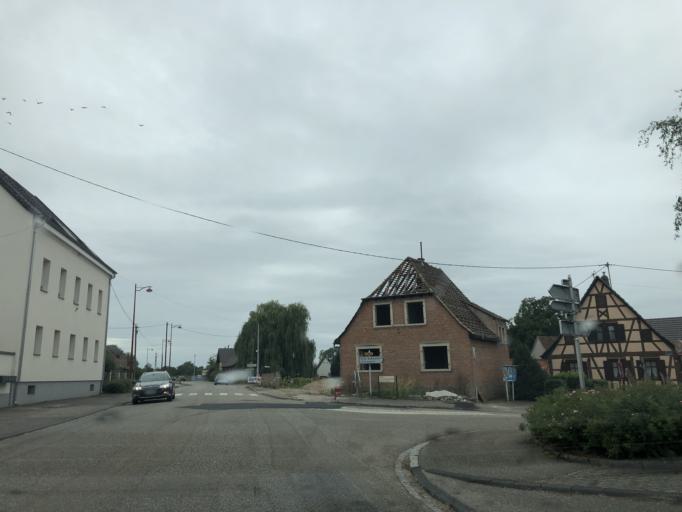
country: DE
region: Rheinland-Pfalz
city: Scheibenhardt
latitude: 48.9767
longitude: 8.1355
